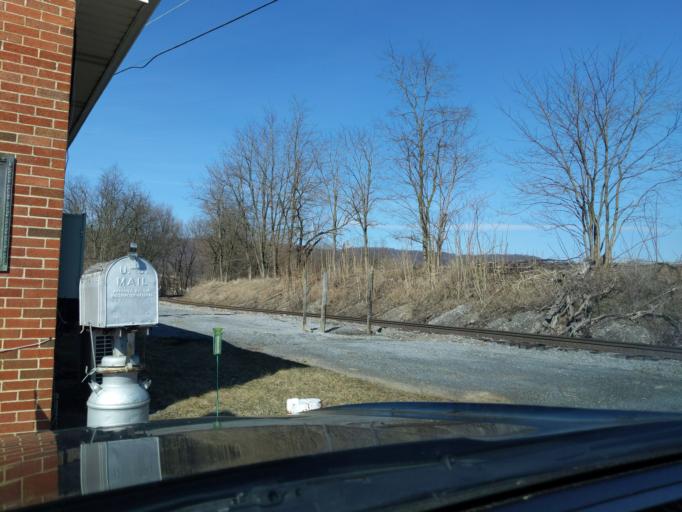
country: US
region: Pennsylvania
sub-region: Blair County
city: Roaring Spring
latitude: 40.3227
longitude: -78.3908
